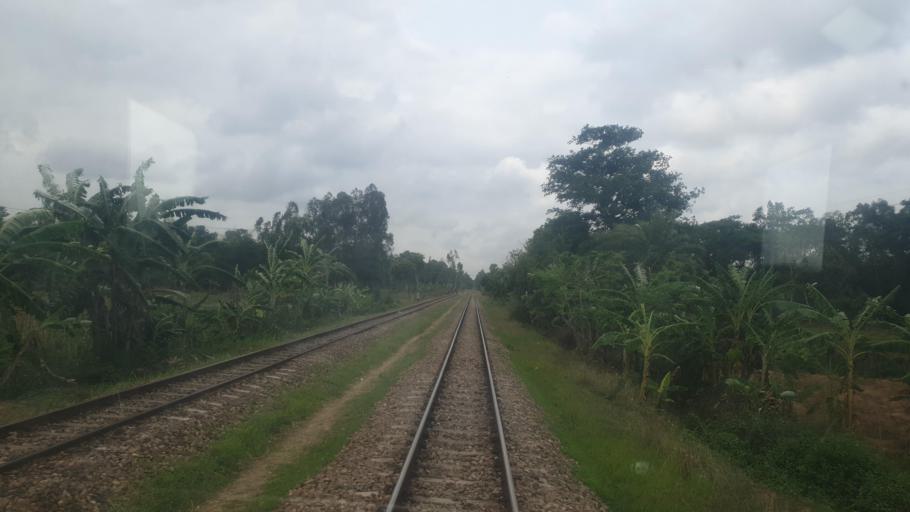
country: BD
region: Chittagong
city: Fatikchari
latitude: 22.6372
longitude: 91.6538
